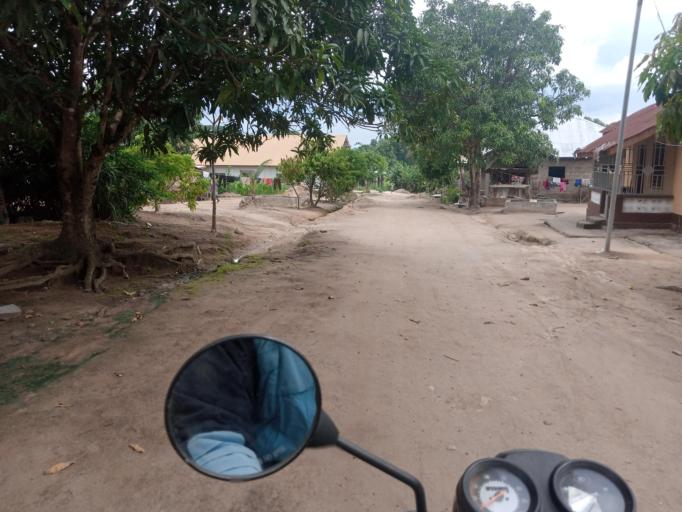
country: SL
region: Southern Province
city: Bo
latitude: 7.9816
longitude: -11.7405
